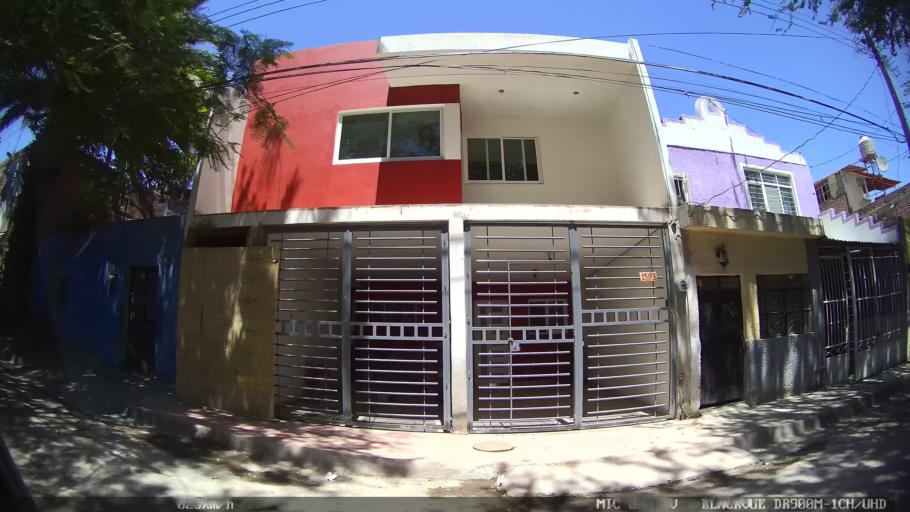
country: MX
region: Jalisco
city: Tlaquepaque
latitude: 20.6846
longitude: -103.2817
